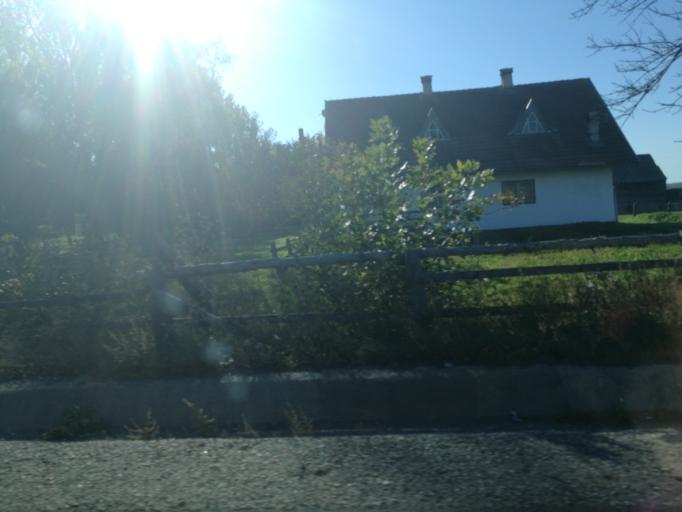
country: RO
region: Brasov
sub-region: Comuna Dumbravita
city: Dumbravita
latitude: 45.7453
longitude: 25.4141
